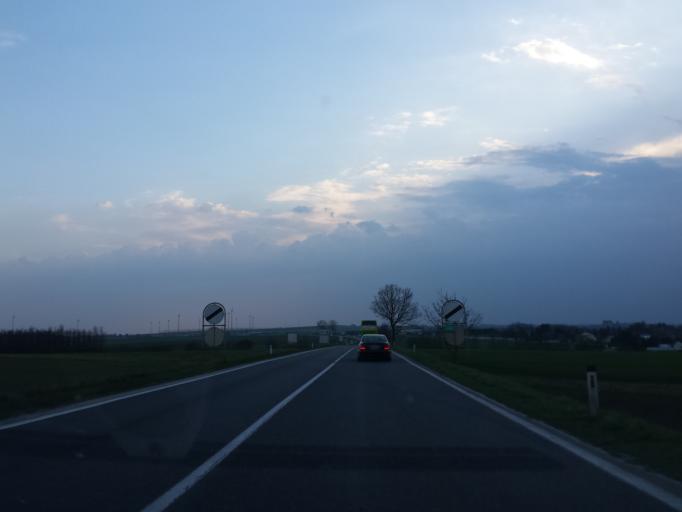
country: AT
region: Lower Austria
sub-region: Politischer Bezirk Mistelbach
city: Wilfersdorf
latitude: 48.5787
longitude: 16.6466
